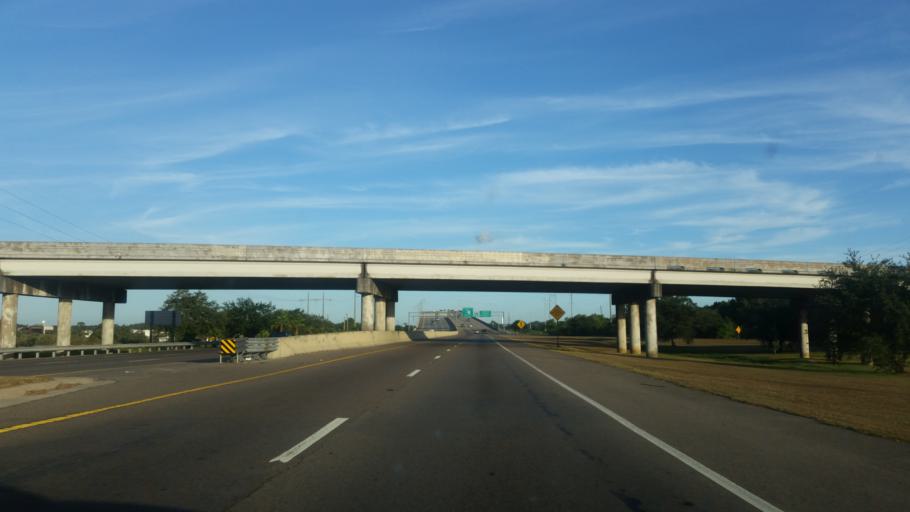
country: US
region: Mississippi
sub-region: Jackson County
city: Pascagoula
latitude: 30.3743
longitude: -88.5717
